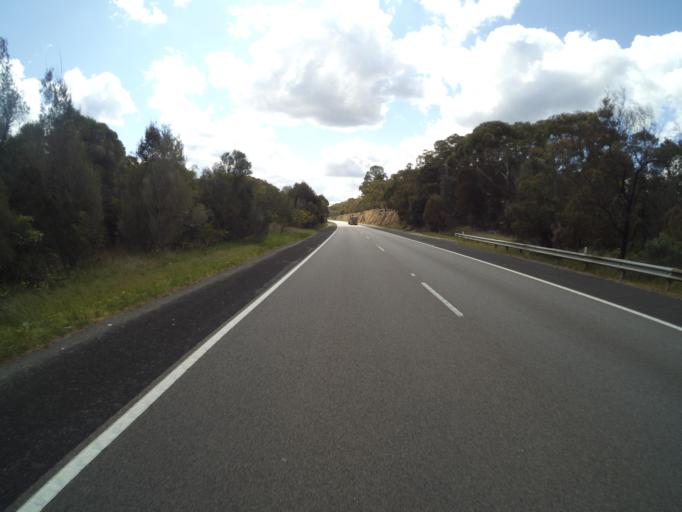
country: AU
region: New South Wales
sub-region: Wingecarribee
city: Colo Vale
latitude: -34.3689
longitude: 150.5384
